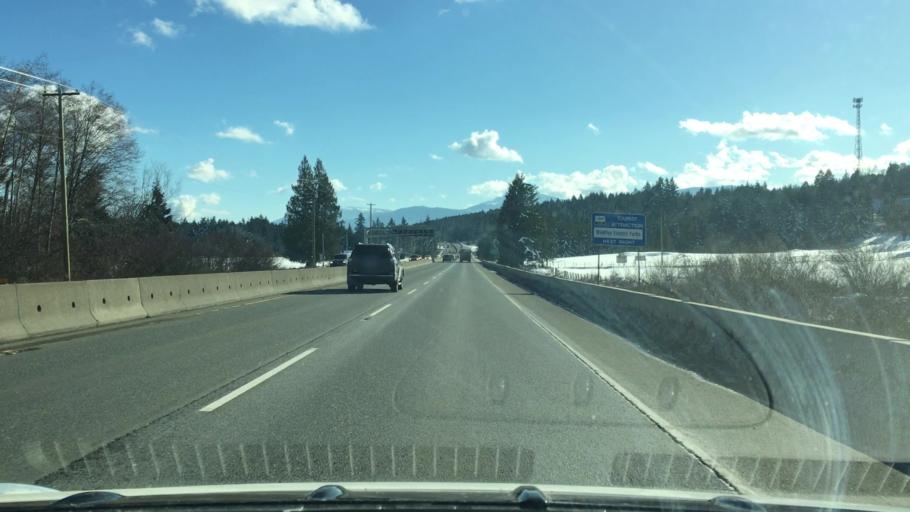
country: CA
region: British Columbia
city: Nanaimo
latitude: 49.0838
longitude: -123.8829
